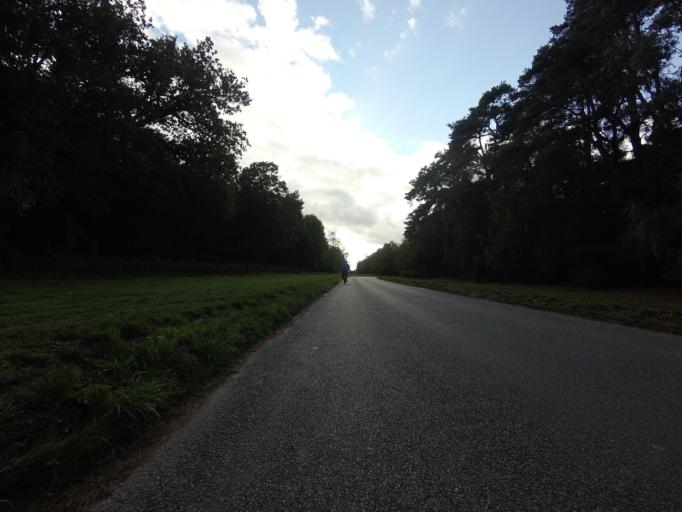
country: GB
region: England
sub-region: Norfolk
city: Dersingham
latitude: 52.8259
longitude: 0.4998
